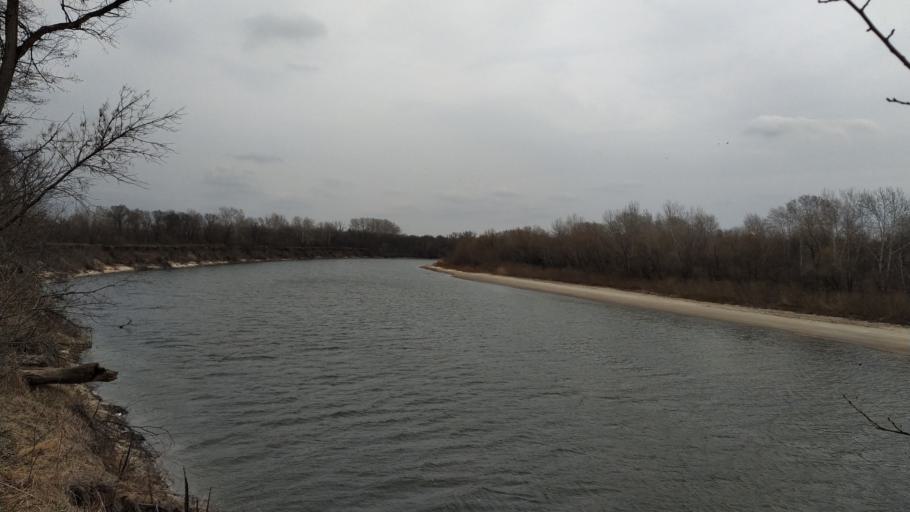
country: RU
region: Rostov
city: Semikarakorsk
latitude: 47.5387
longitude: 40.6819
